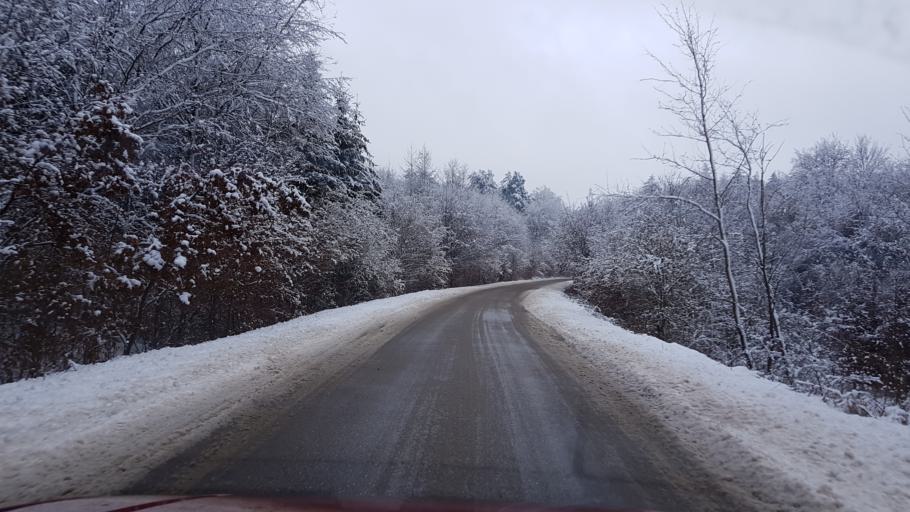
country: PL
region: West Pomeranian Voivodeship
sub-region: Powiat drawski
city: Zlocieniec
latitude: 53.5043
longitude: 15.9989
